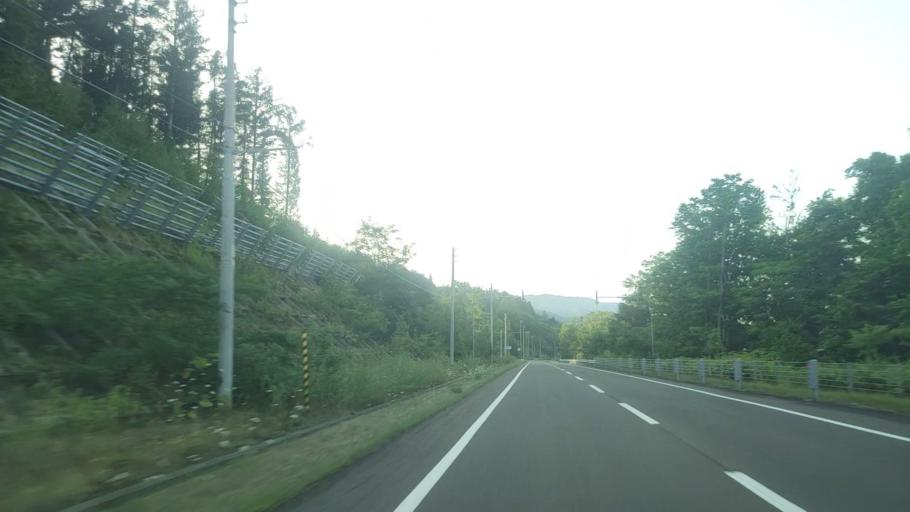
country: JP
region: Hokkaido
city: Bibai
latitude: 43.0717
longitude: 142.1039
